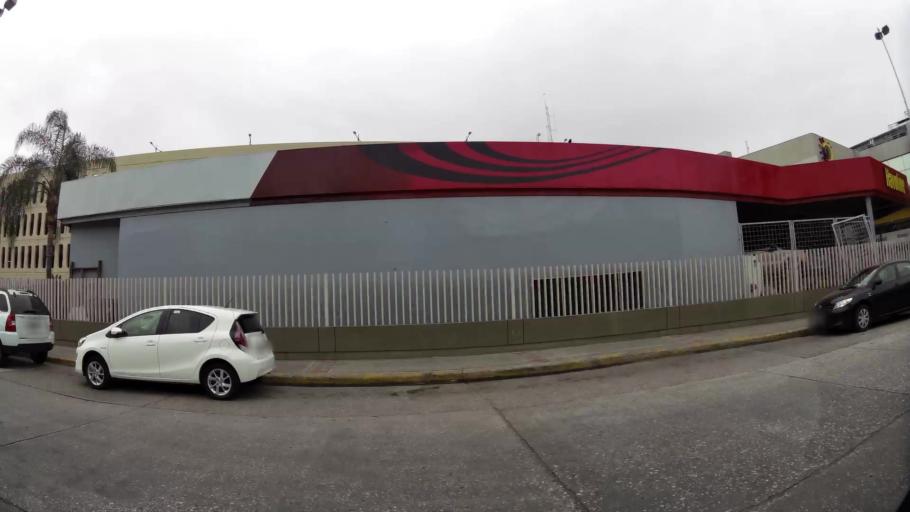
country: EC
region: Guayas
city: Eloy Alfaro
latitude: -2.1545
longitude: -79.8924
